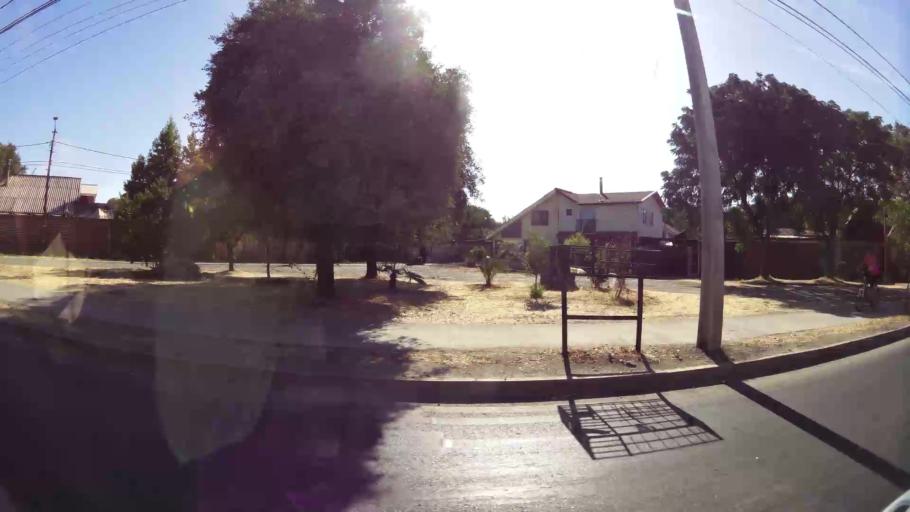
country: CL
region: Maule
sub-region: Provincia de Talca
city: Talca
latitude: -35.4262
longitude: -71.6756
